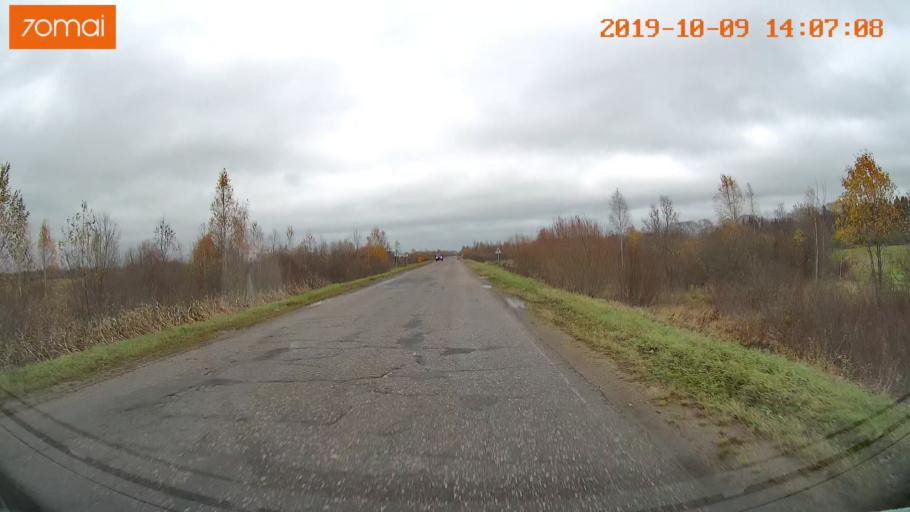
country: RU
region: Kostroma
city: Buy
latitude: 58.4686
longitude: 41.4188
